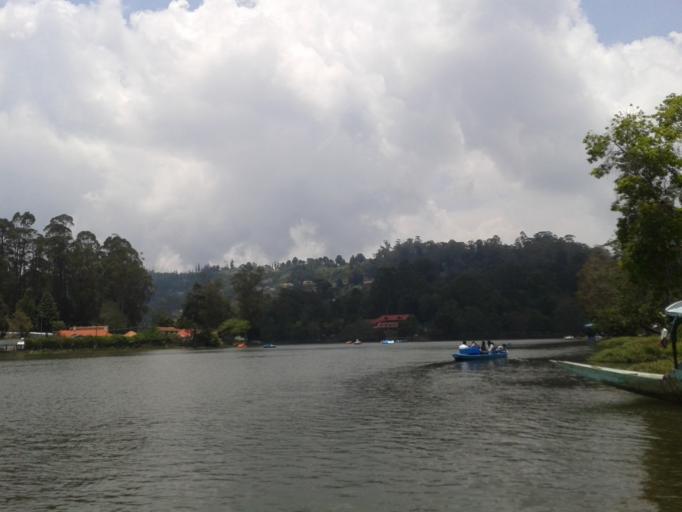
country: IN
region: Tamil Nadu
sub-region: Dindigul
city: Kodaikanal
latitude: 10.2333
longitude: 77.4890
